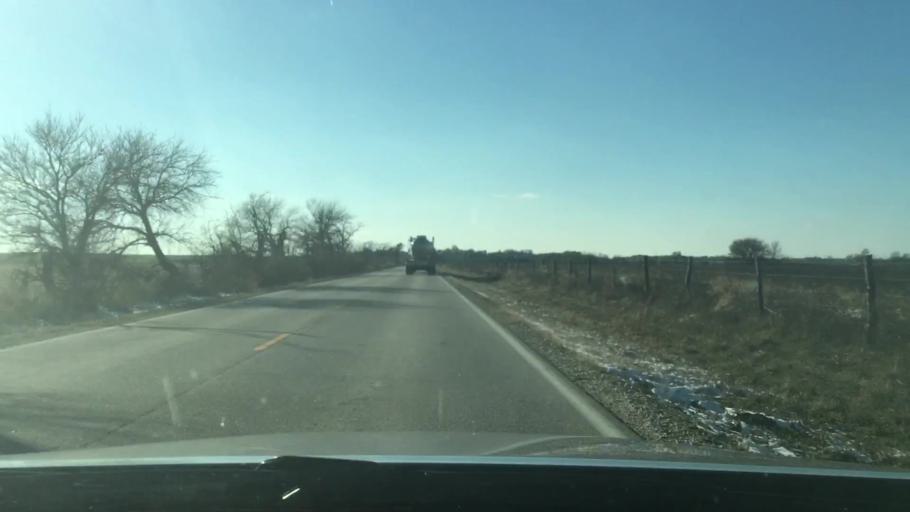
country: US
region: Kansas
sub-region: Reno County
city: Nickerson
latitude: 38.1449
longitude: -98.1255
